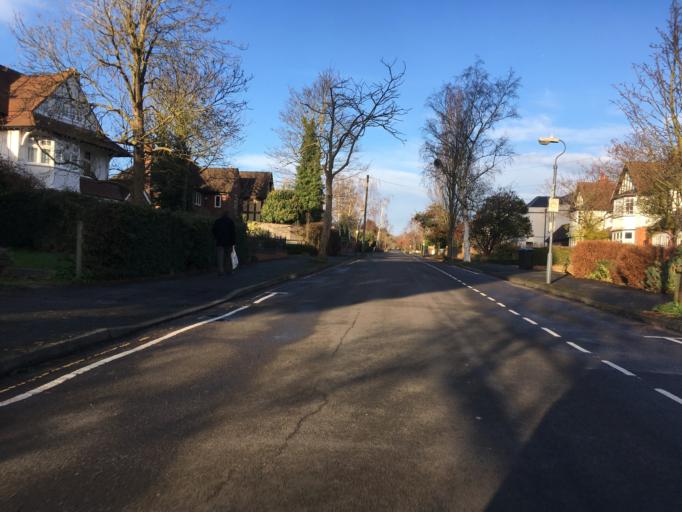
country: GB
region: England
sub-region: Warwickshire
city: Stratford-upon-Avon
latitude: 52.1989
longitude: -1.7043
